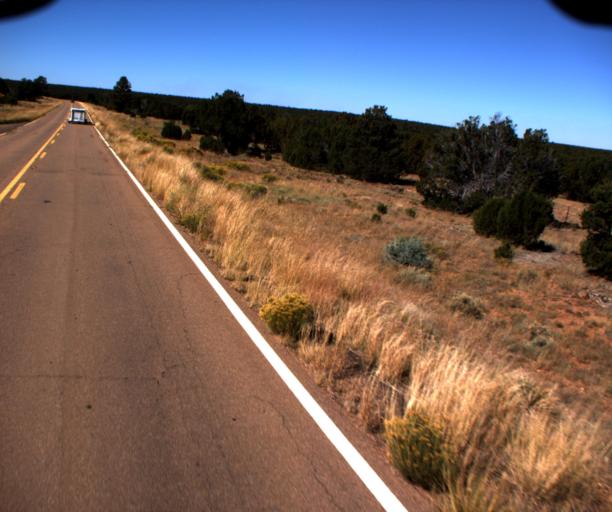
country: US
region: Arizona
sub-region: Navajo County
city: Heber-Overgaard
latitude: 34.4605
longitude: -110.5047
